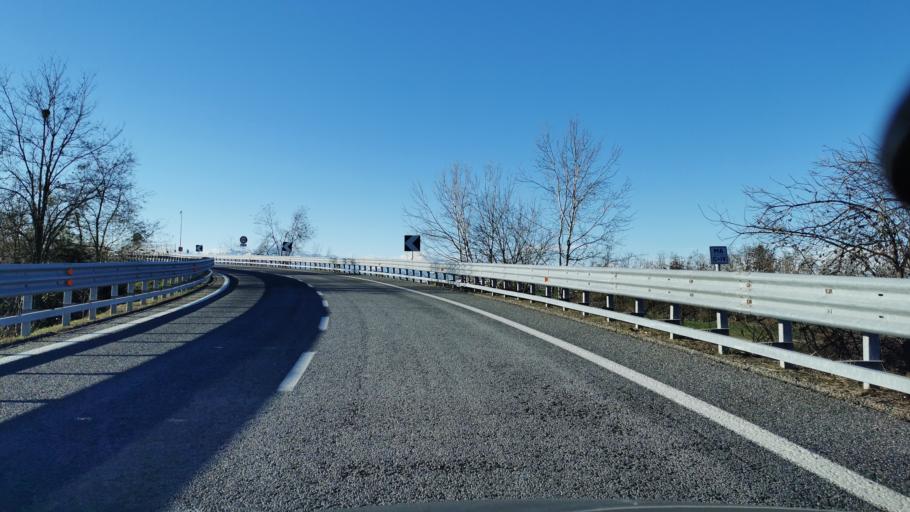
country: IT
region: Piedmont
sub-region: Provincia di Cuneo
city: Magliano Alpi
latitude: 44.4901
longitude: 7.8186
